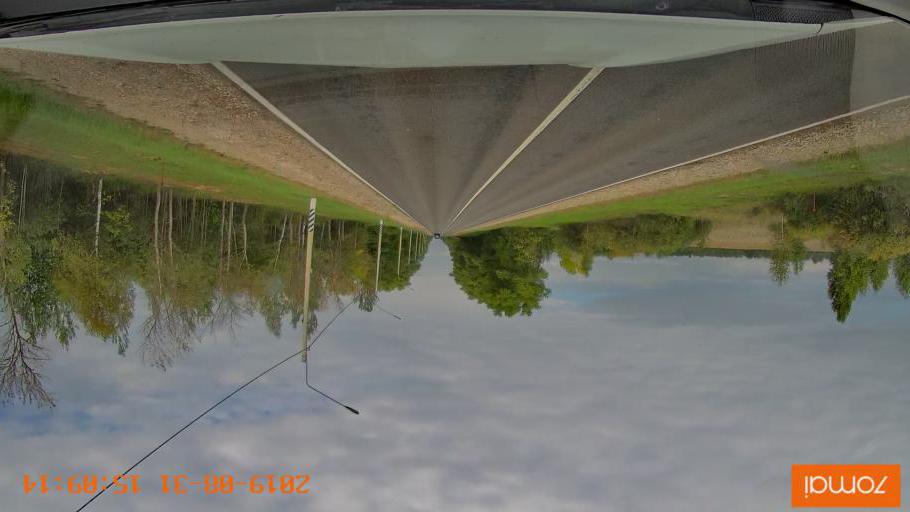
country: RU
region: Kaluga
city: Spas-Demensk
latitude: 54.3996
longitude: 34.1969
